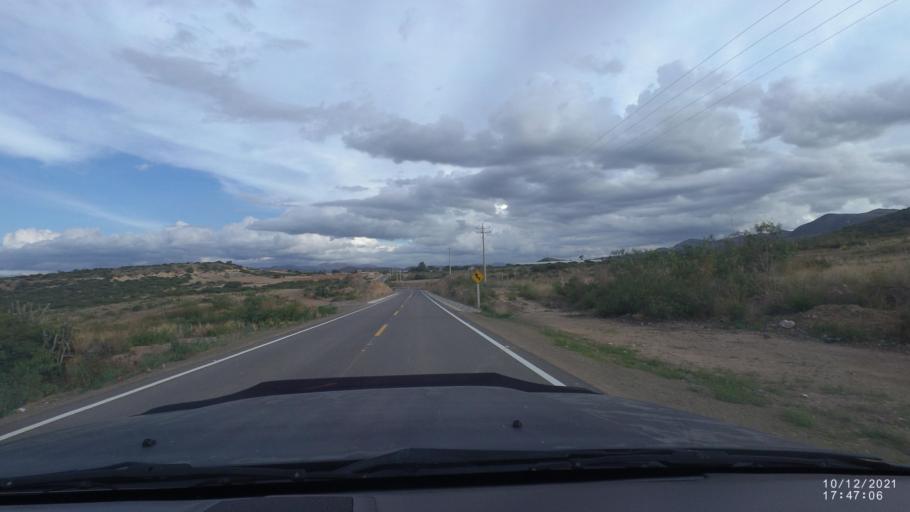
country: BO
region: Cochabamba
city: Tarata
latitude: -17.6356
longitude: -65.9884
